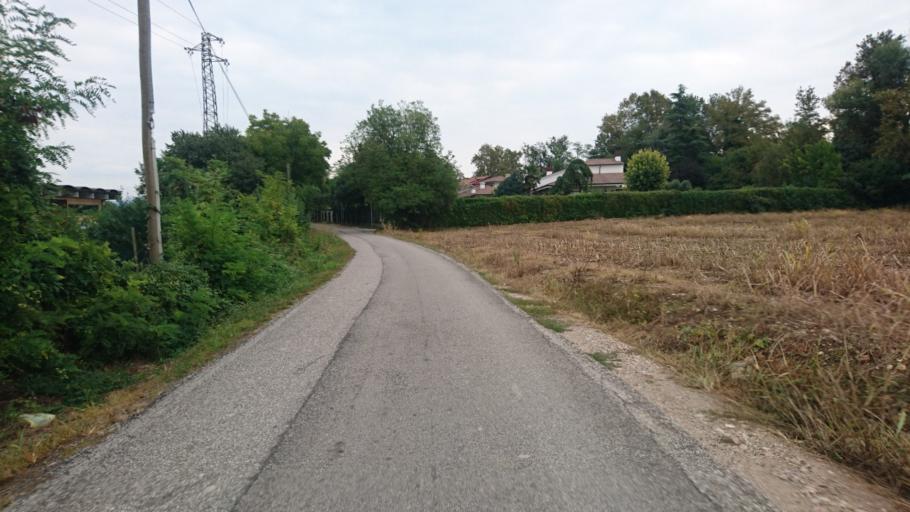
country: IT
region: Veneto
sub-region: Provincia di Verona
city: San Martino Buon Albergo
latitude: 45.4087
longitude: 11.0776
